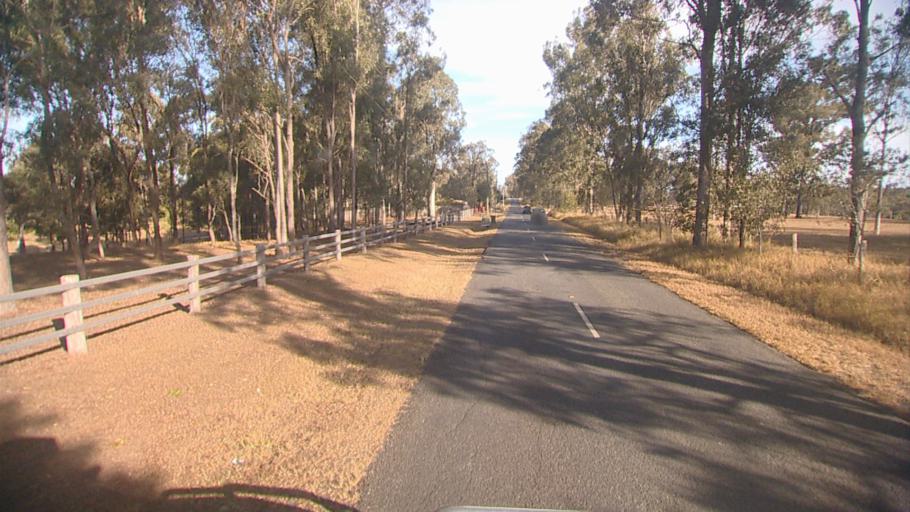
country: AU
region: Queensland
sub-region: Logan
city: Cedar Vale
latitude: -27.8686
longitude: 153.0113
